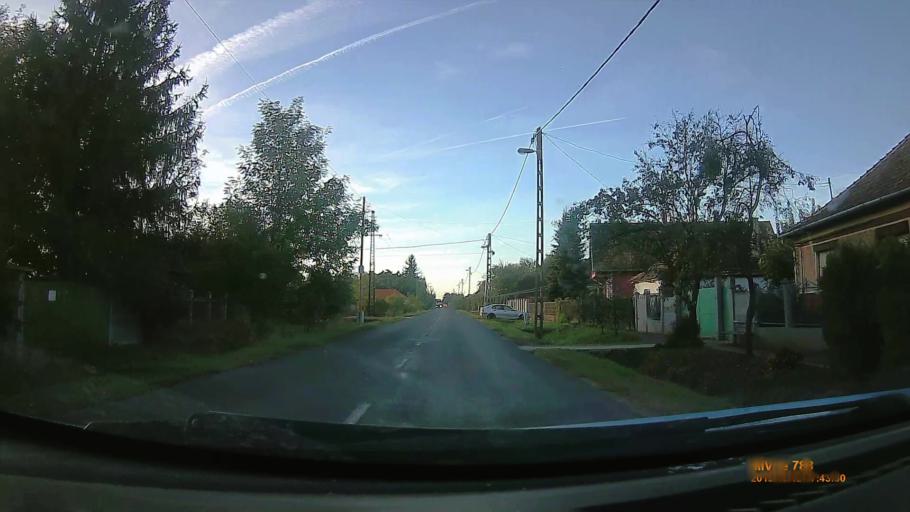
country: RO
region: Bihor
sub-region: Comuna Bors
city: Bors
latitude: 47.1906
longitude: 21.7876
